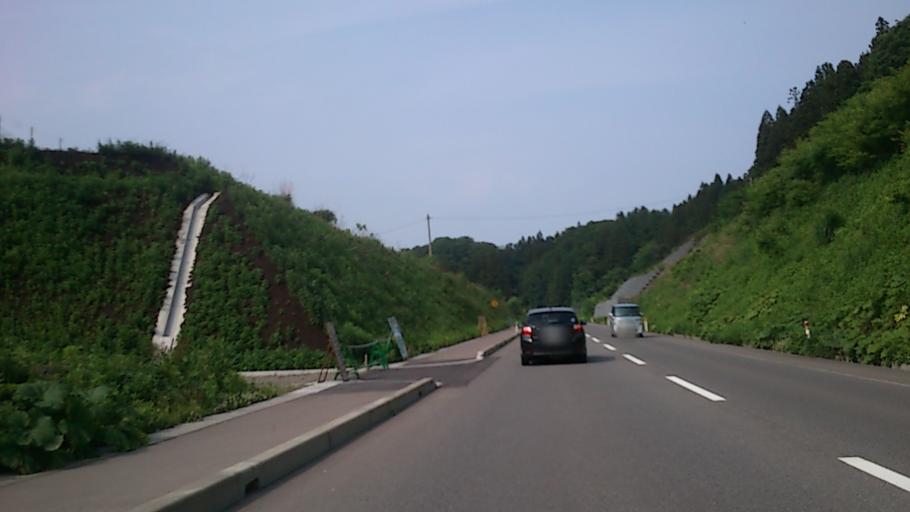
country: JP
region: Aomori
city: Hirosaki
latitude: 40.5707
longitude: 140.2967
